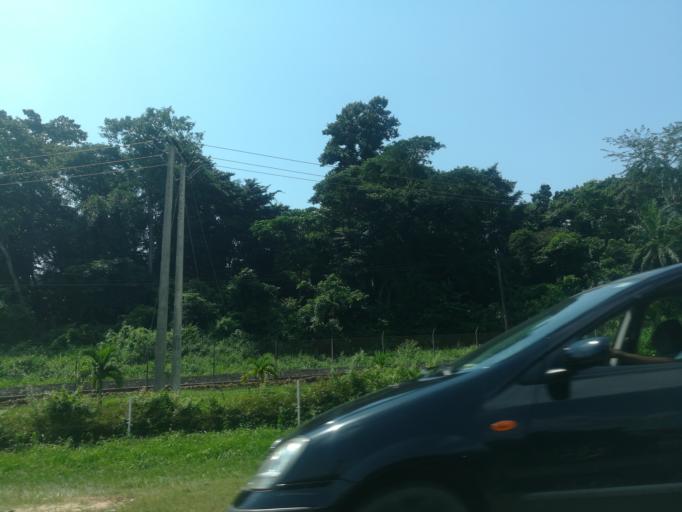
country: NG
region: Oyo
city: Moniya
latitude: 7.4936
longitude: 3.9146
